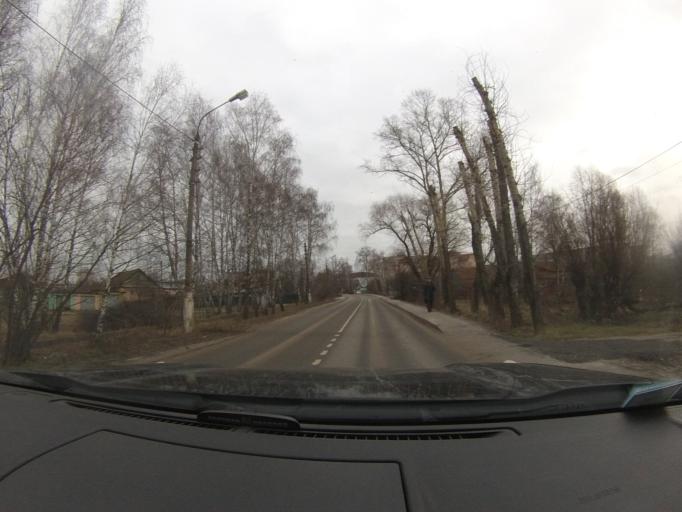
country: RU
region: Moskovskaya
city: Lopatinskiy
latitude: 55.3251
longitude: 38.6992
